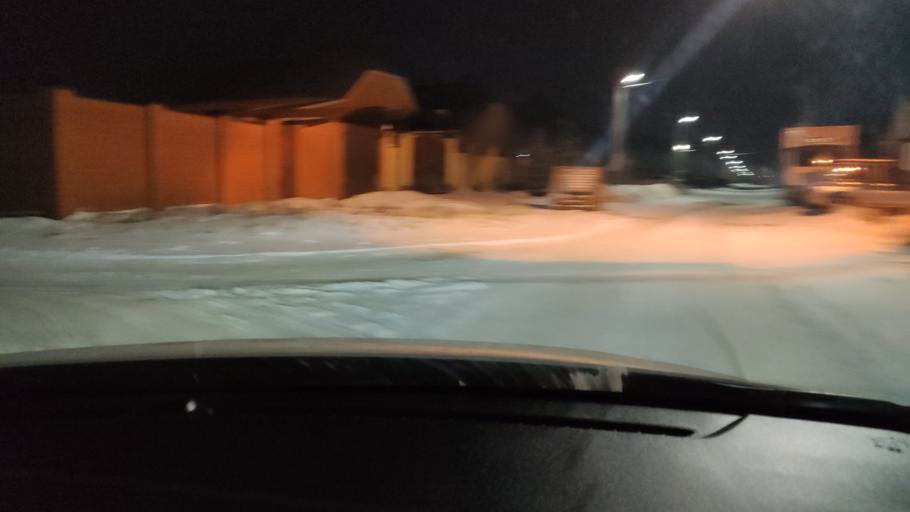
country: RU
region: Tatarstan
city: Vysokaya Gora
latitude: 55.8396
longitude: 49.2416
